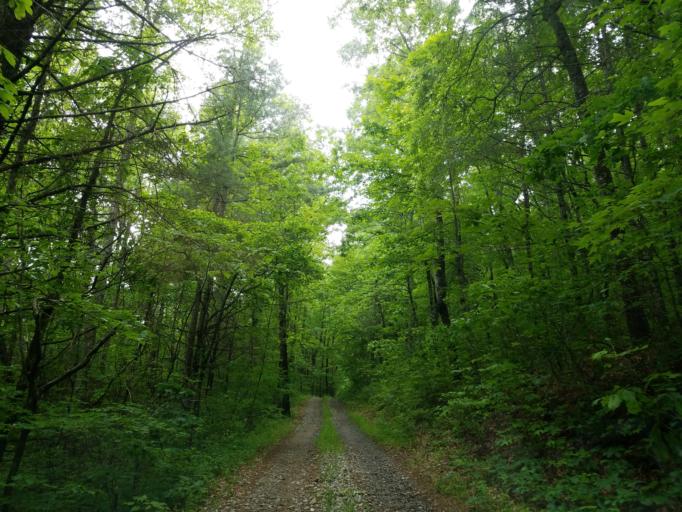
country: US
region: Georgia
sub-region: Union County
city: Blairsville
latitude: 34.7512
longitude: -84.0056
